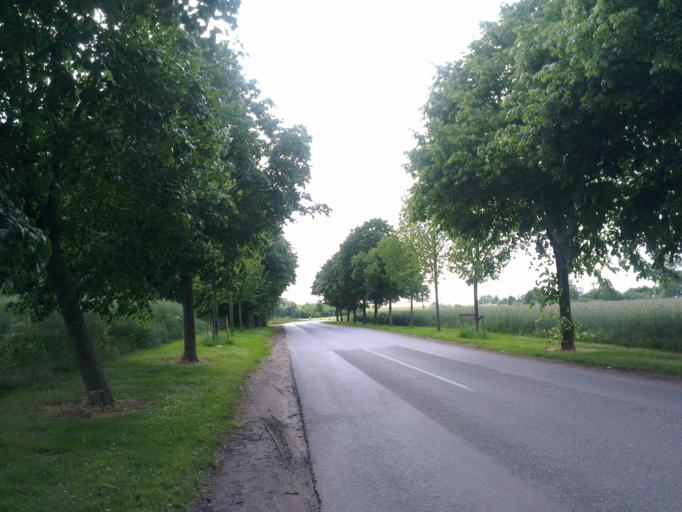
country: DK
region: Capital Region
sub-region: Frederikssund Kommune
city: Skibby
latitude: 55.7281
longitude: 11.9462
